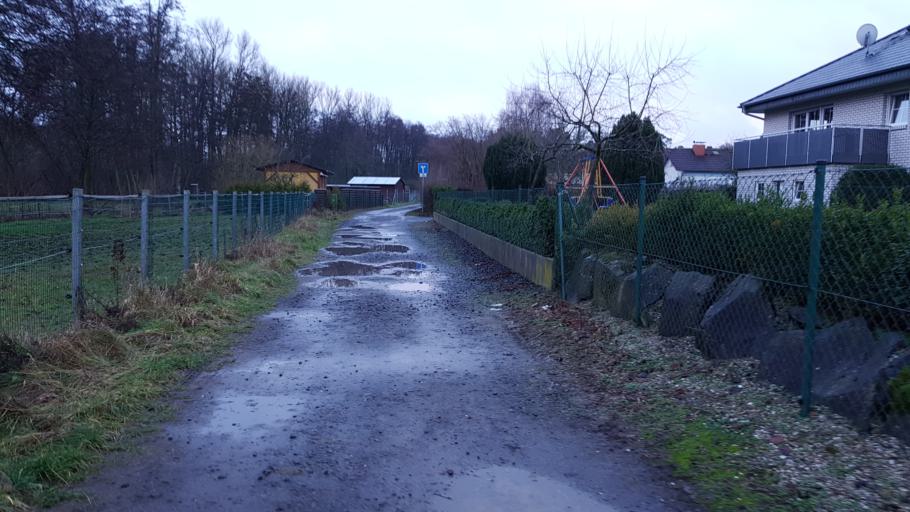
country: DE
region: Hesse
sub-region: Regierungsbezirk Giessen
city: Grunberg
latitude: 50.6438
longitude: 9.0342
